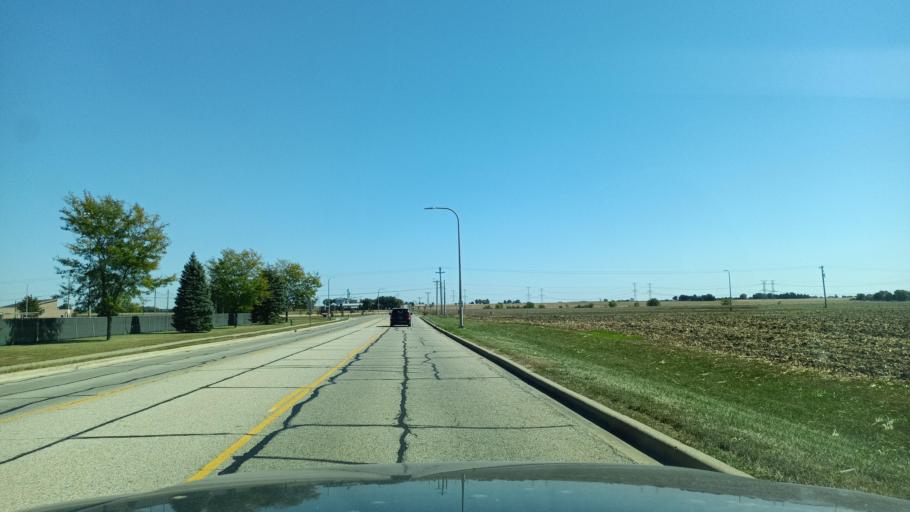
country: US
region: Illinois
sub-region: Tazewell County
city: Morton
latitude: 40.6133
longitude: -89.4335
